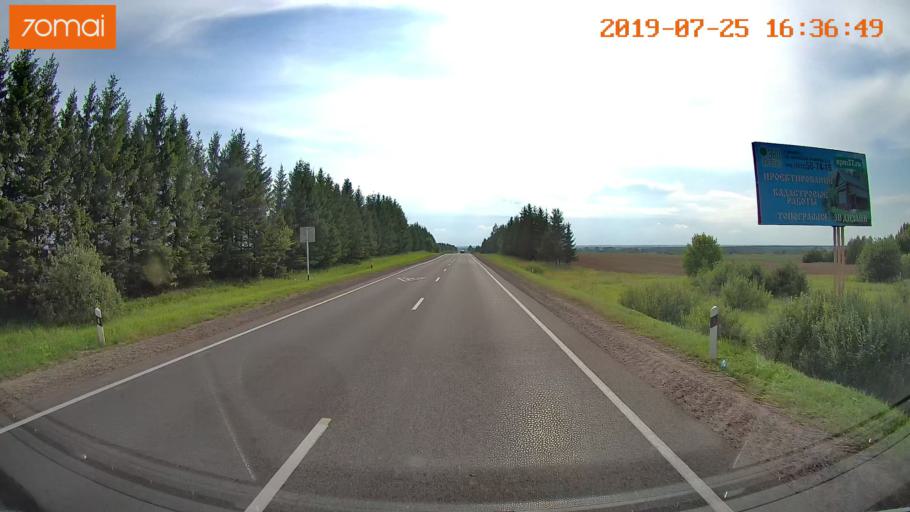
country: RU
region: Ivanovo
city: Privolzhsk
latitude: 57.3939
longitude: 41.3919
